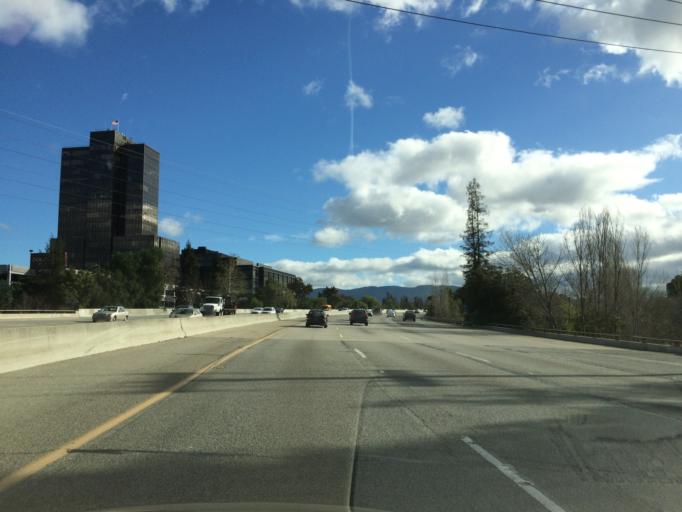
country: US
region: California
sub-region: Santa Clara County
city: Campbell
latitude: 37.2910
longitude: -121.9368
